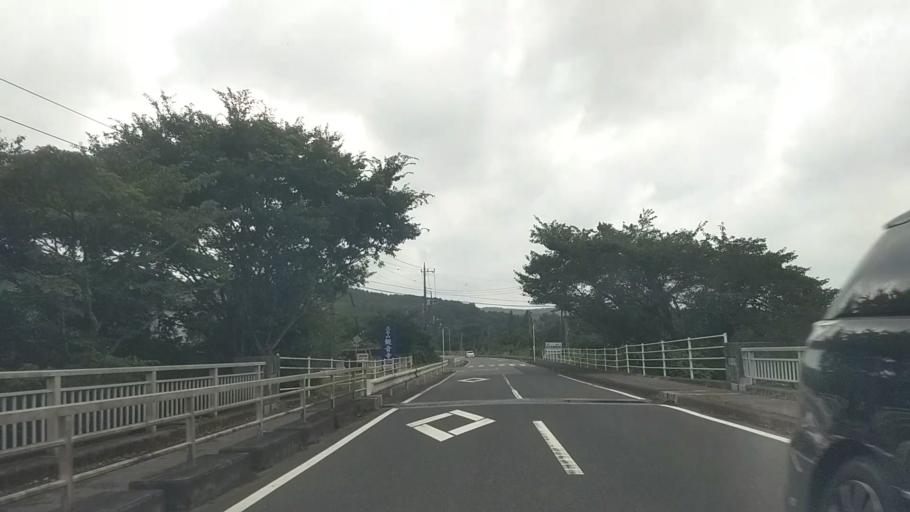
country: JP
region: Chiba
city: Kawaguchi
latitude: 35.2273
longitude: 140.0959
